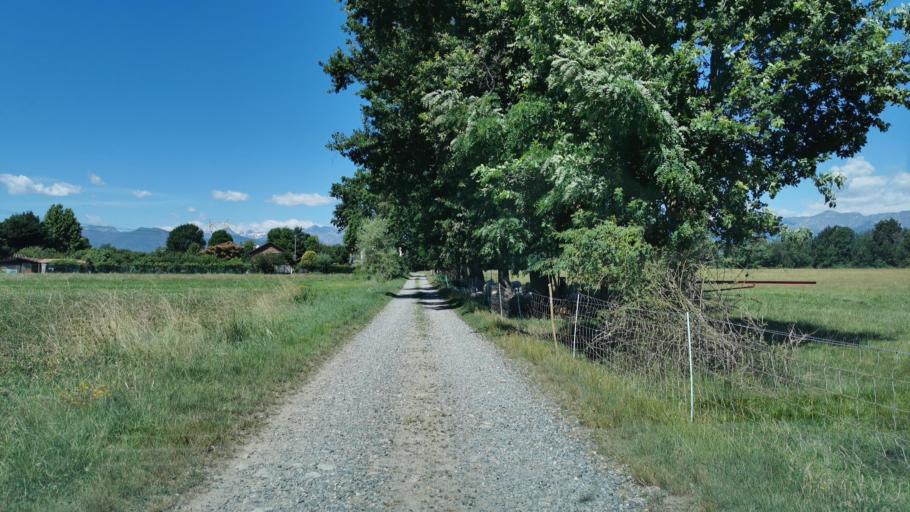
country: IT
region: Piedmont
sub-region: Provincia di Torino
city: San Francesco al Campo
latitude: 45.2339
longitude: 7.6840
